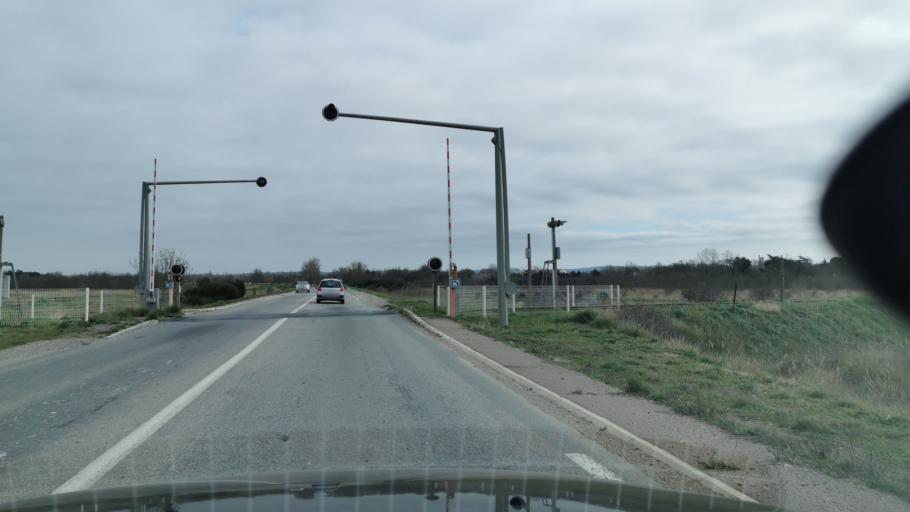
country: FR
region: Languedoc-Roussillon
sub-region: Departement de l'Aude
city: Narbonne
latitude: 43.1938
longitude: 2.9844
